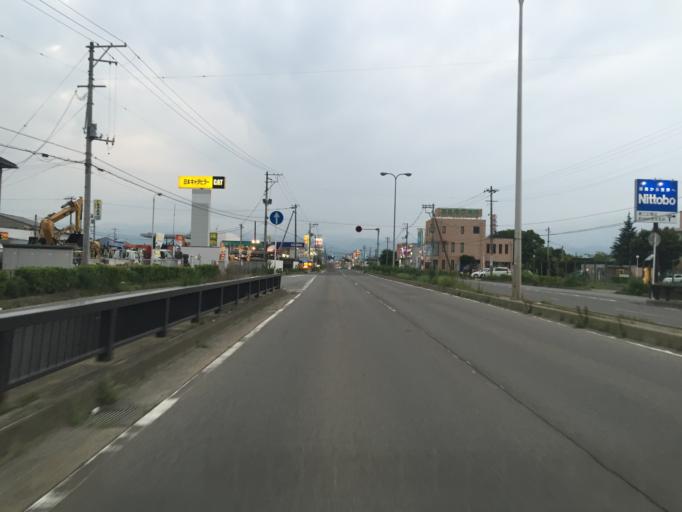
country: JP
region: Fukushima
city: Fukushima-shi
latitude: 37.7395
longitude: 140.4563
